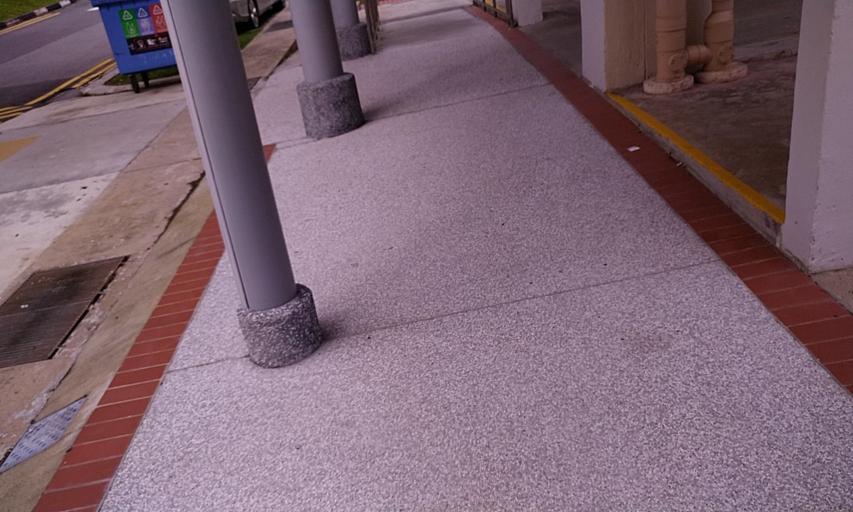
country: SG
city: Singapore
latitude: 1.2887
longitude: 103.8138
